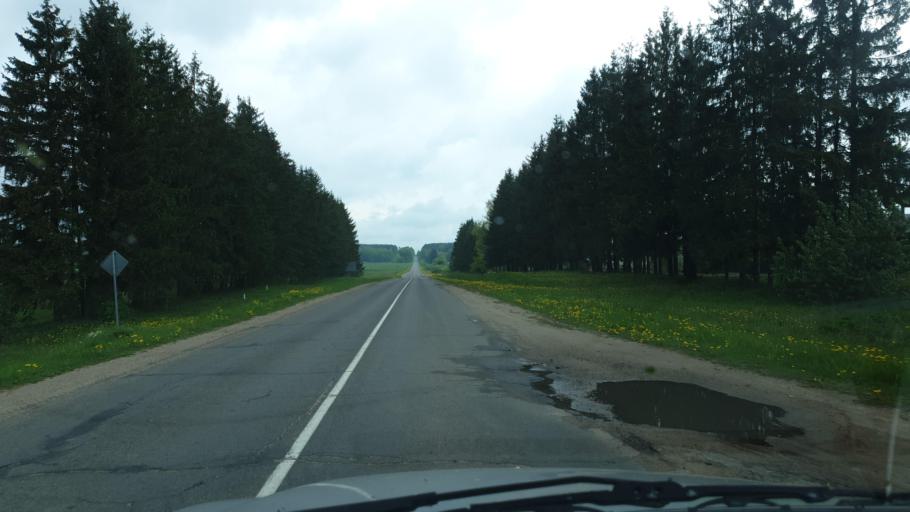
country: BY
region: Vitebsk
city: Lyepyel'
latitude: 54.8890
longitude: 28.6195
